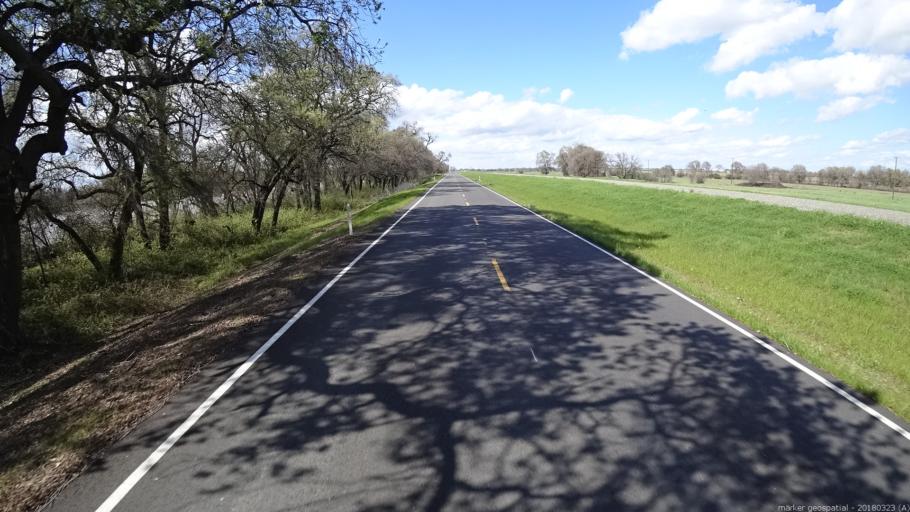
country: US
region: California
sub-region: Yolo County
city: West Sacramento
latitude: 38.6522
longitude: -121.5994
